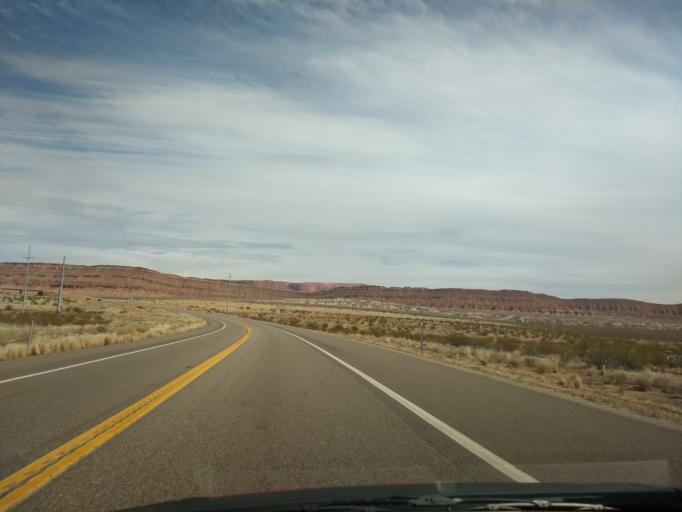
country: US
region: Utah
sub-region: Washington County
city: Washington
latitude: 37.0209
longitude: -113.4890
